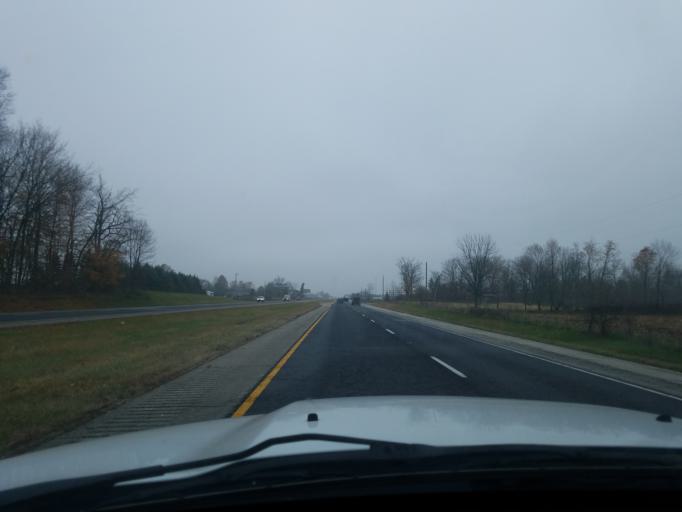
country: US
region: Indiana
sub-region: Hamilton County
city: Westfield
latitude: 40.1079
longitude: -86.1279
